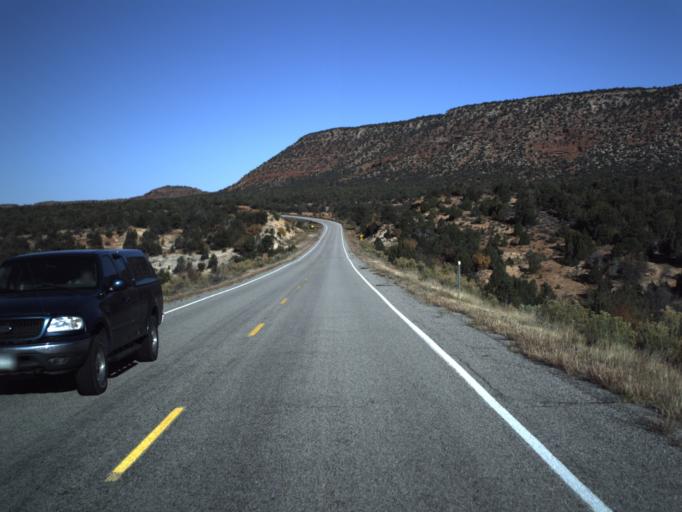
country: US
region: Utah
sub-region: San Juan County
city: Blanding
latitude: 37.5828
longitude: -109.8909
